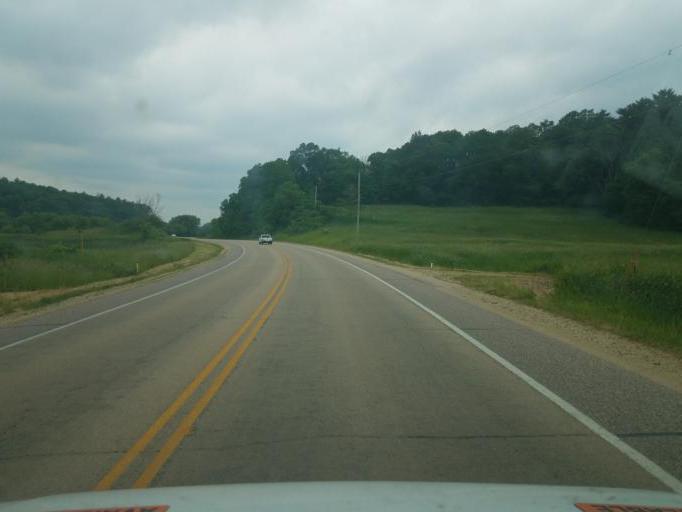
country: US
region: Wisconsin
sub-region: Juneau County
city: Elroy
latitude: 43.6417
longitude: -90.2029
